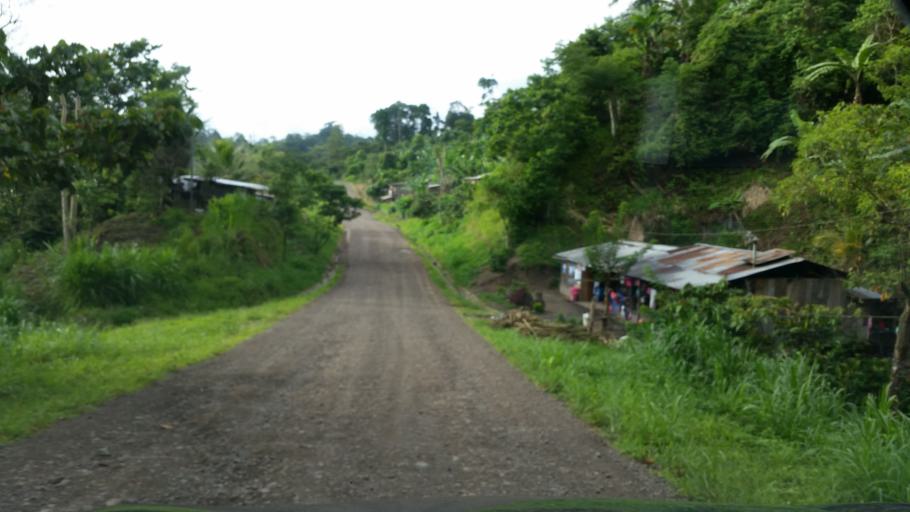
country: NI
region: Jinotega
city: Jinotega
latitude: 13.2551
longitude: -85.7371
